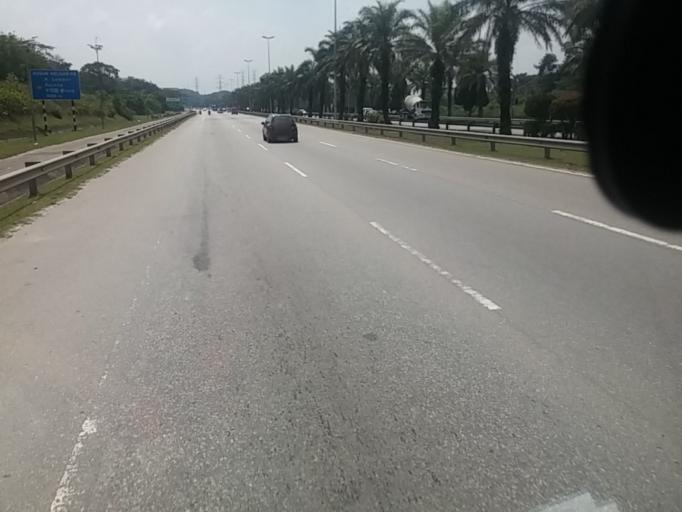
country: MY
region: Putrajaya
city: Putrajaya
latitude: 2.9642
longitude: 101.6614
